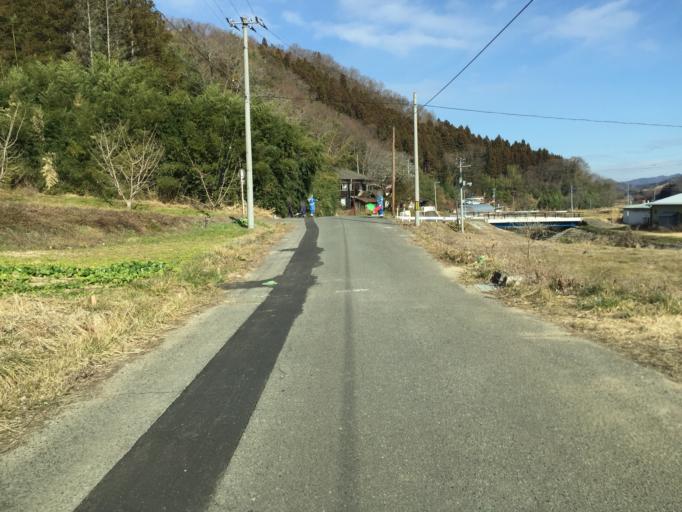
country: JP
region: Fukushima
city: Hobaramachi
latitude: 37.7483
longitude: 140.5638
